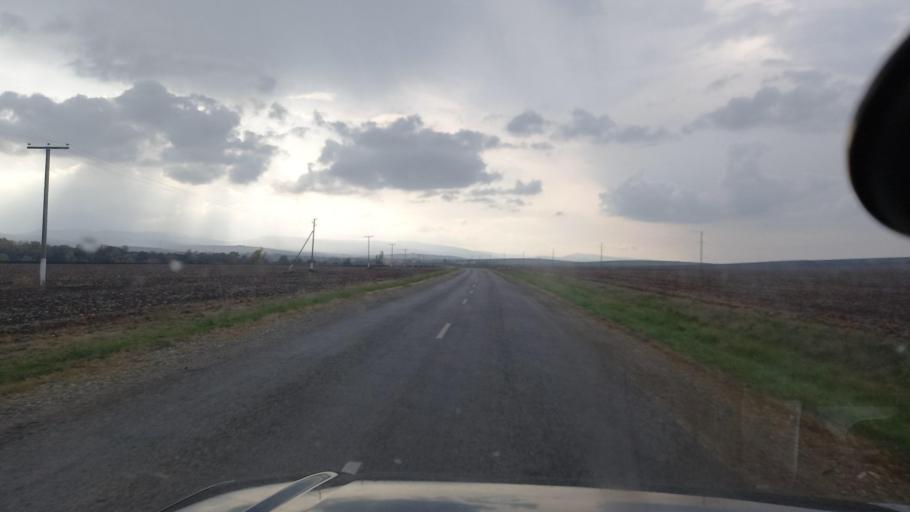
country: RU
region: Krasnodarskiy
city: Gubskaya
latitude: 44.3483
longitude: 40.6901
